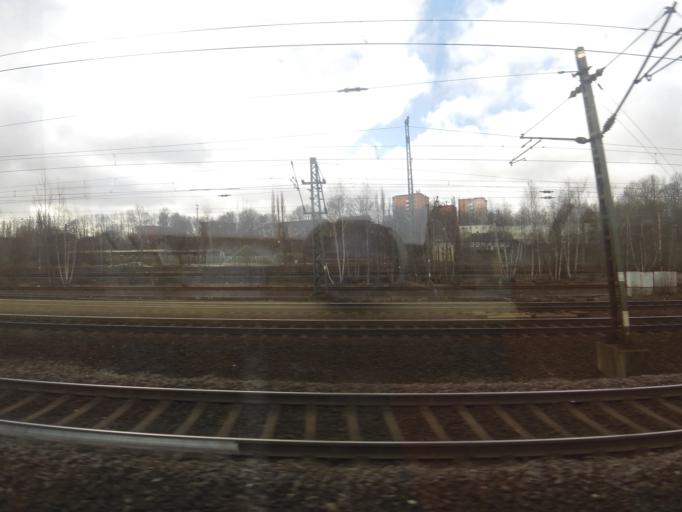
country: DE
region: Hamburg
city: Harburg
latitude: 53.4458
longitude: 10.0043
